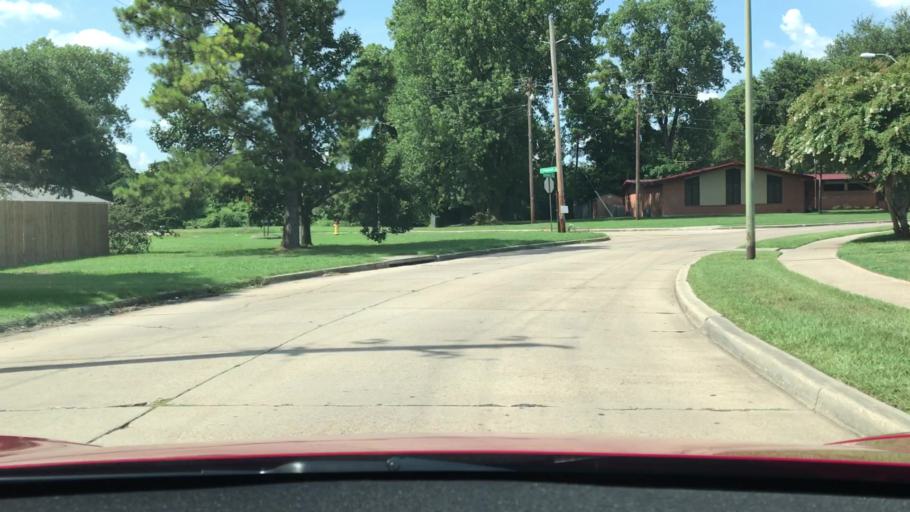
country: US
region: Louisiana
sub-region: Bossier Parish
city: Bossier City
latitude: 32.4776
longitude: -93.7286
